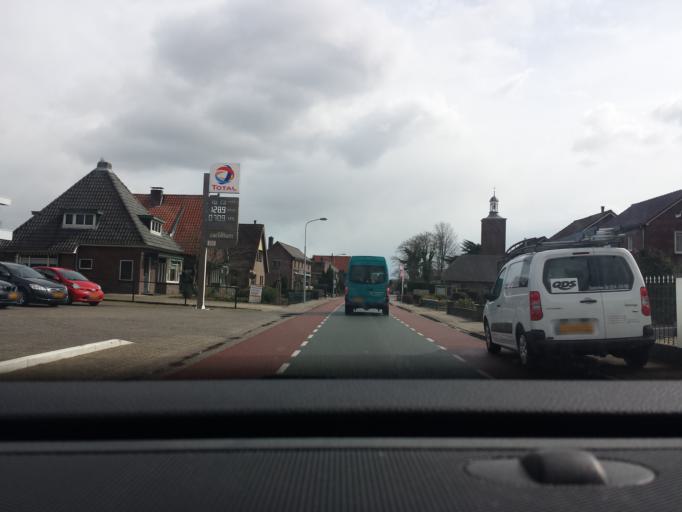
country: NL
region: Gelderland
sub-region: Oude IJsselstreek
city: Varsseveld
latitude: 51.9916
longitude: 6.4261
